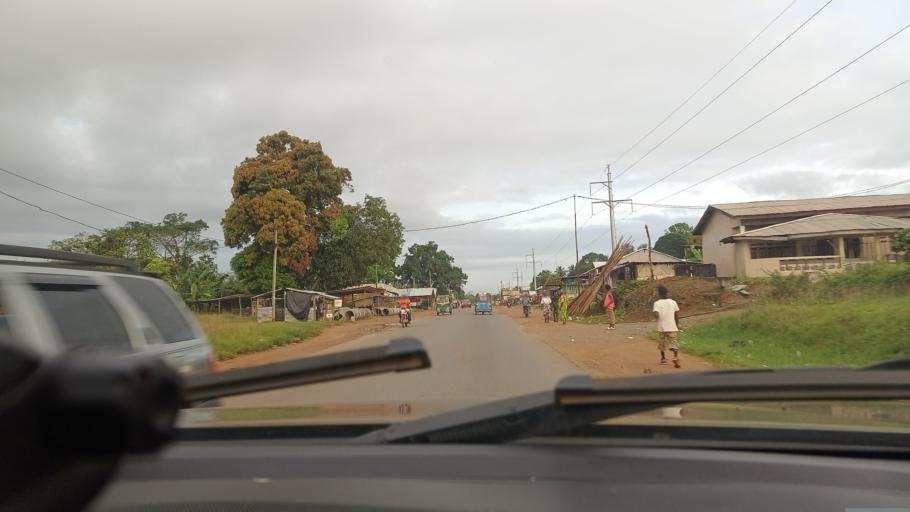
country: LR
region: Montserrado
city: Monrovia
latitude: 6.4463
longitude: -10.7996
